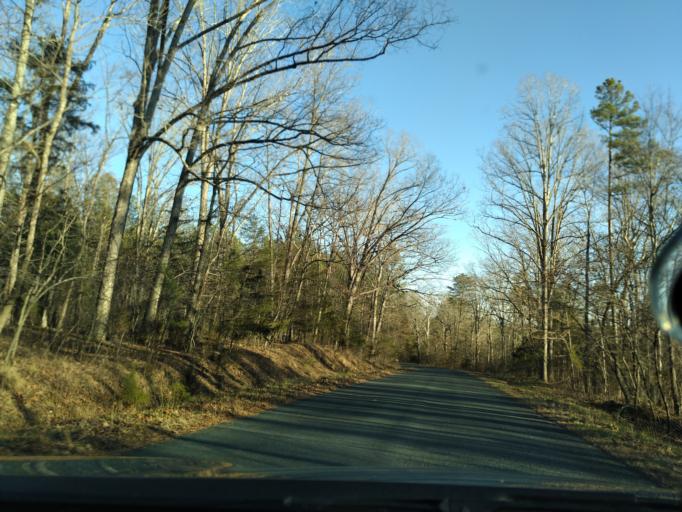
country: US
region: Virginia
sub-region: Appomattox County
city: Appomattox
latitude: 37.3830
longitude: -78.6502
